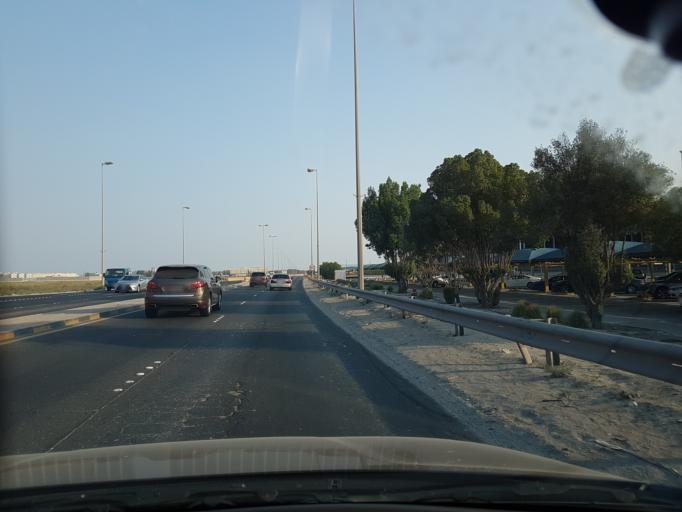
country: BH
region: Northern
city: Sitrah
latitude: 26.0946
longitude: 50.6087
